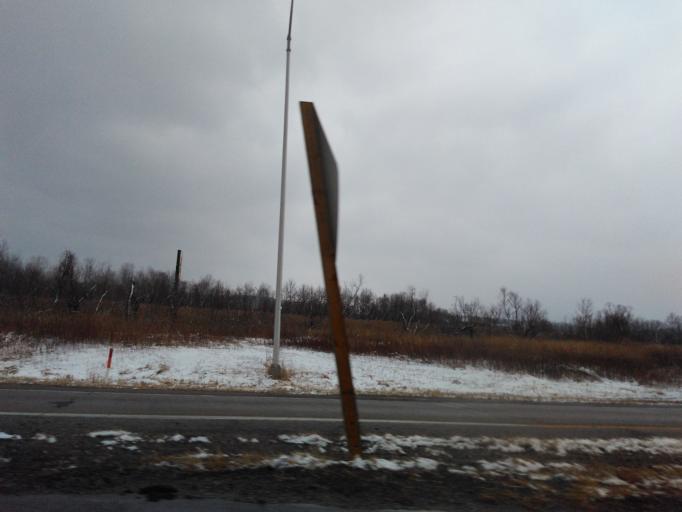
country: US
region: Illinois
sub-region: Saint Clair County
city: Alorton
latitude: 38.5848
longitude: -90.1043
